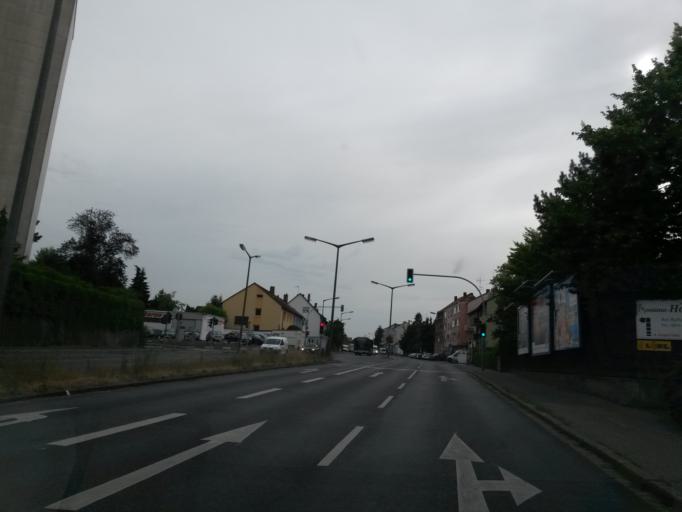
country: DE
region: Bavaria
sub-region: Regierungsbezirk Mittelfranken
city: Oberasbach
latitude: 49.4369
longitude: 10.9806
